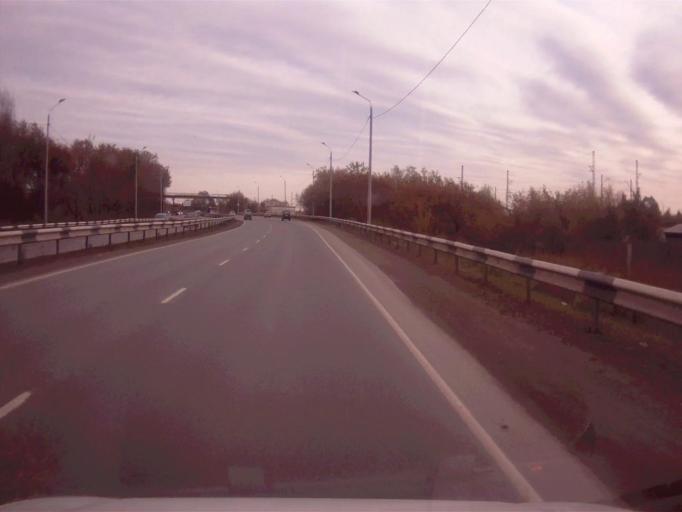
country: RU
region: Chelyabinsk
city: Novosineglazovskiy
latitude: 55.0437
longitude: 61.4238
